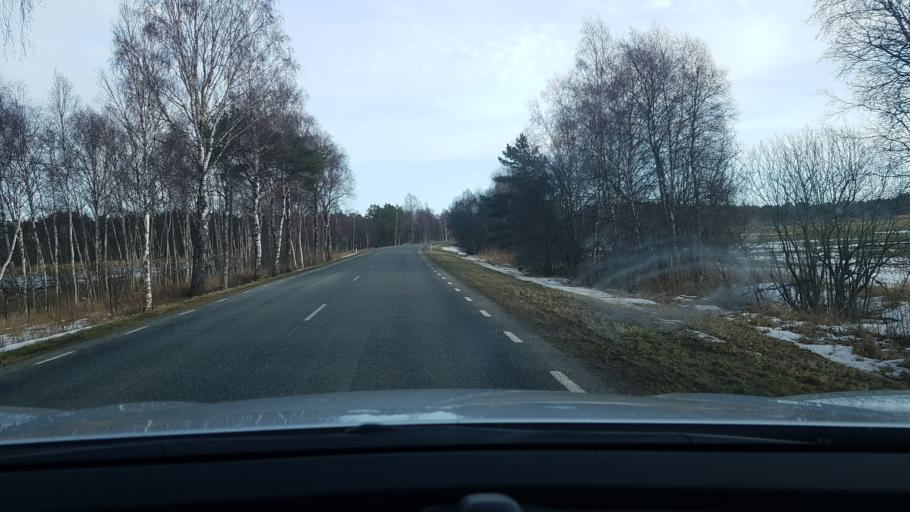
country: EE
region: Saare
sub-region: Kuressaare linn
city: Kuressaare
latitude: 58.4269
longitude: 22.6784
